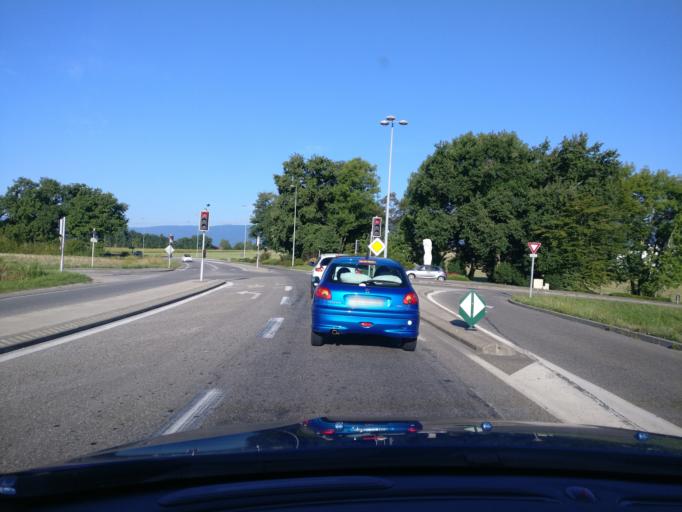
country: FR
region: Rhone-Alpes
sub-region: Departement de l'Ain
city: Ferney-Voltaire
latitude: 46.2496
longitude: 6.1023
